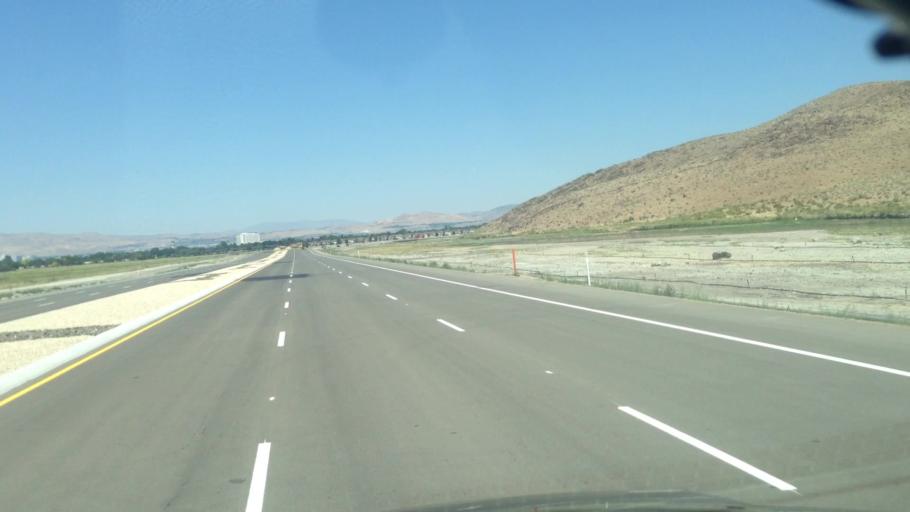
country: US
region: Nevada
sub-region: Washoe County
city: Sparks
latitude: 39.4697
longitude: -119.7324
